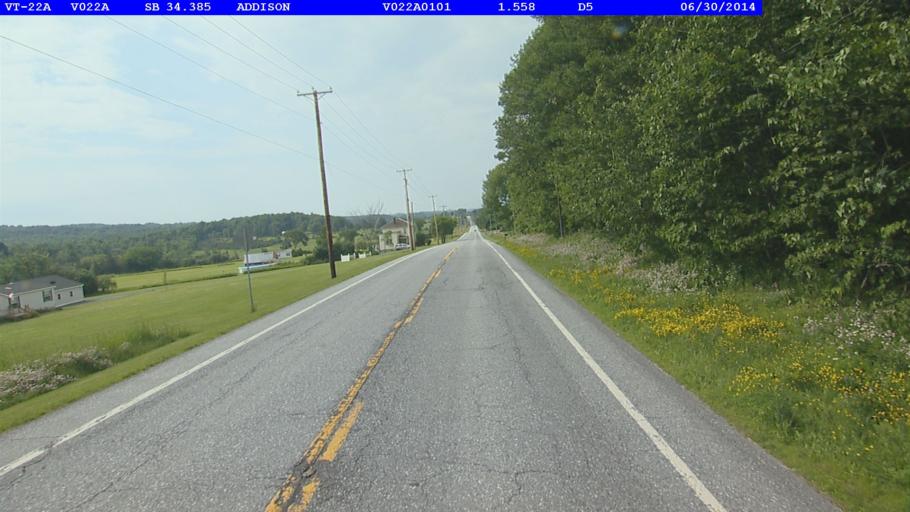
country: US
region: Vermont
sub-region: Addison County
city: Vergennes
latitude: 44.0520
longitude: -73.3015
